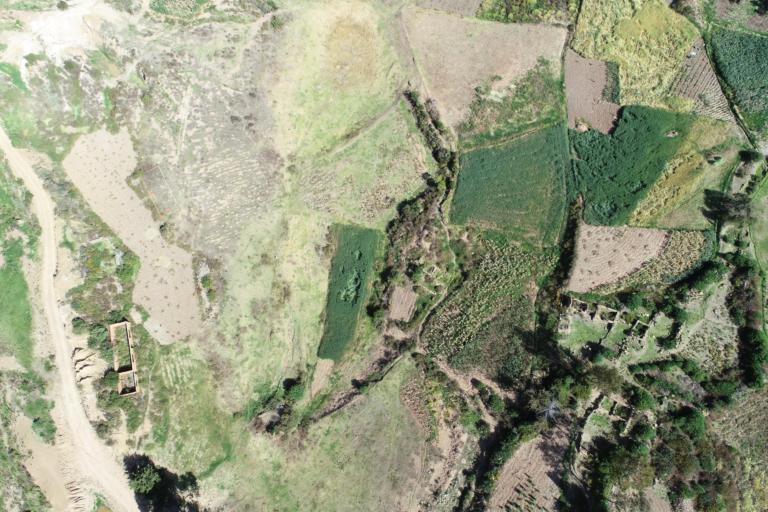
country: BO
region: La Paz
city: La Paz
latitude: -16.5550
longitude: -67.9885
